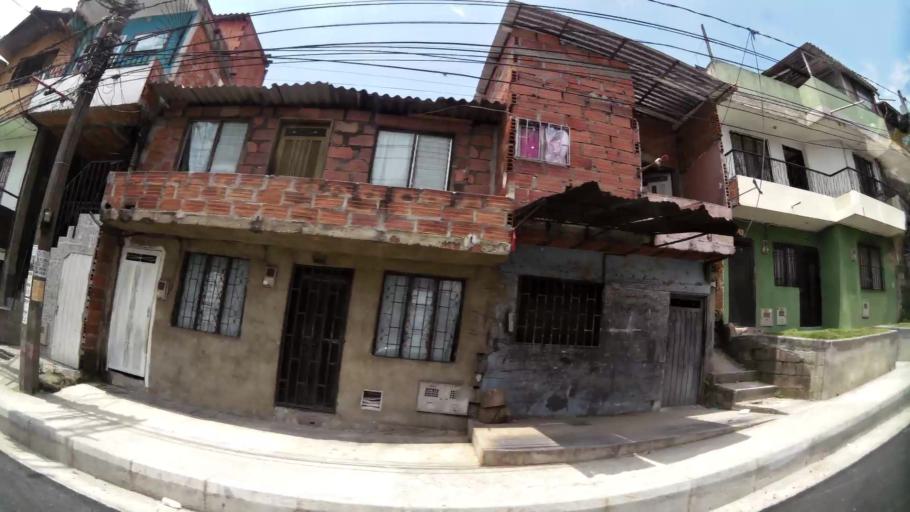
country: CO
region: Antioquia
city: Medellin
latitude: 6.2927
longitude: -75.5825
